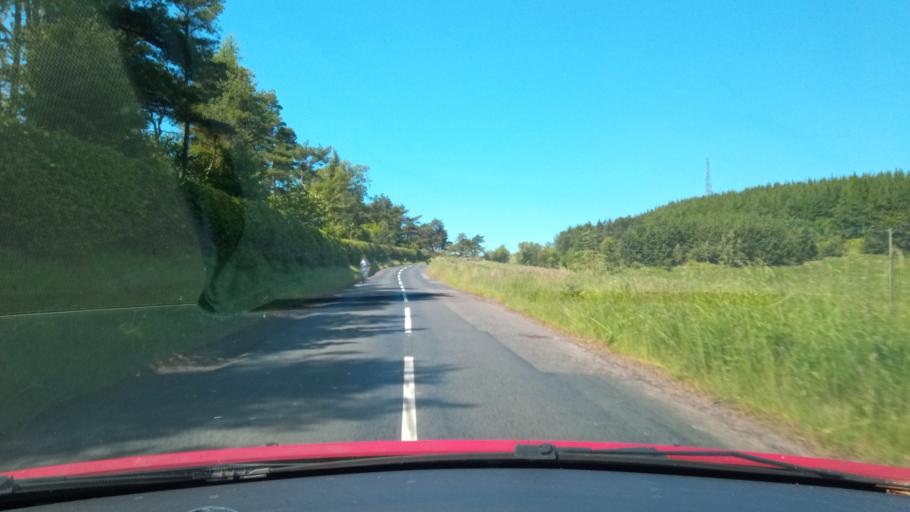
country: GB
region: Scotland
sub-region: The Scottish Borders
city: Duns
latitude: 55.7781
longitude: -2.4106
